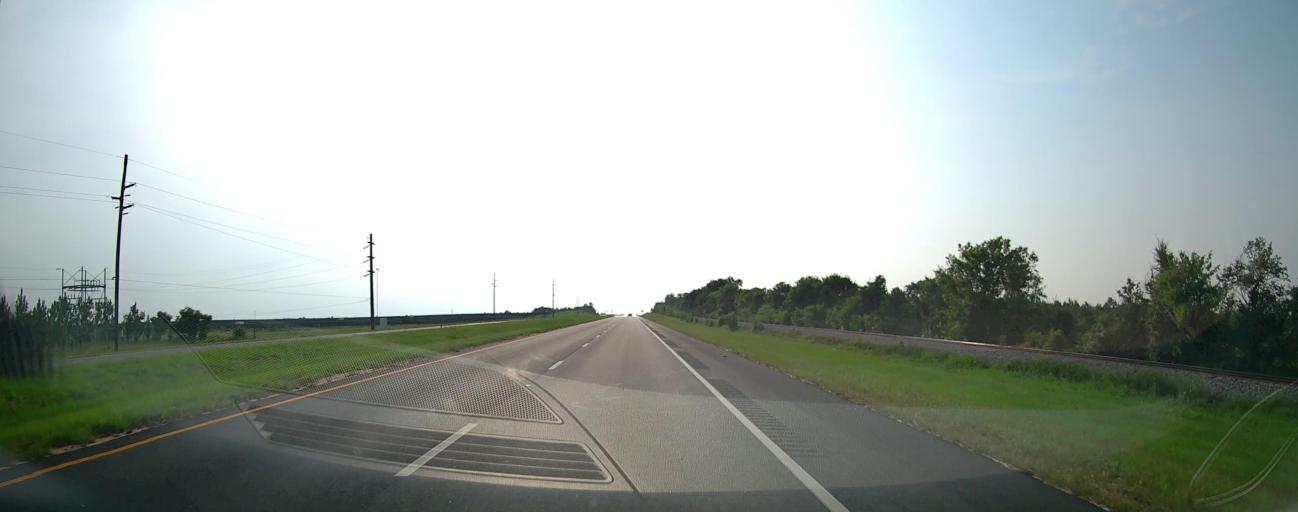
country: US
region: Georgia
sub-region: Taylor County
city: Butler
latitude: 32.5775
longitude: -84.3108
